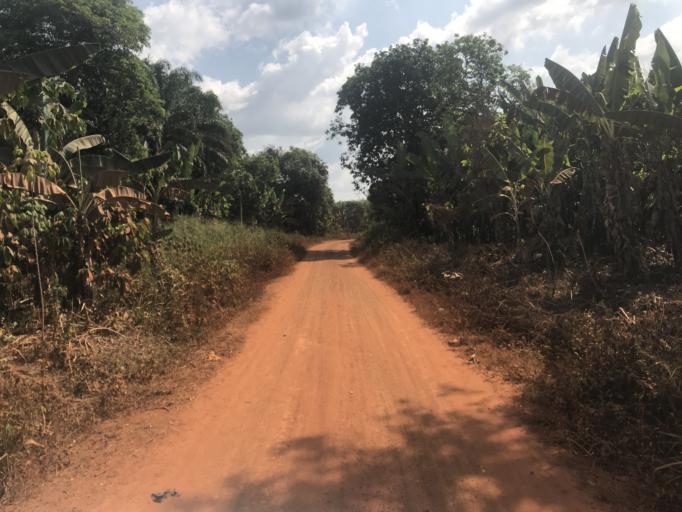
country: NG
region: Osun
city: Ibokun
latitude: 7.7998
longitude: 4.6870
